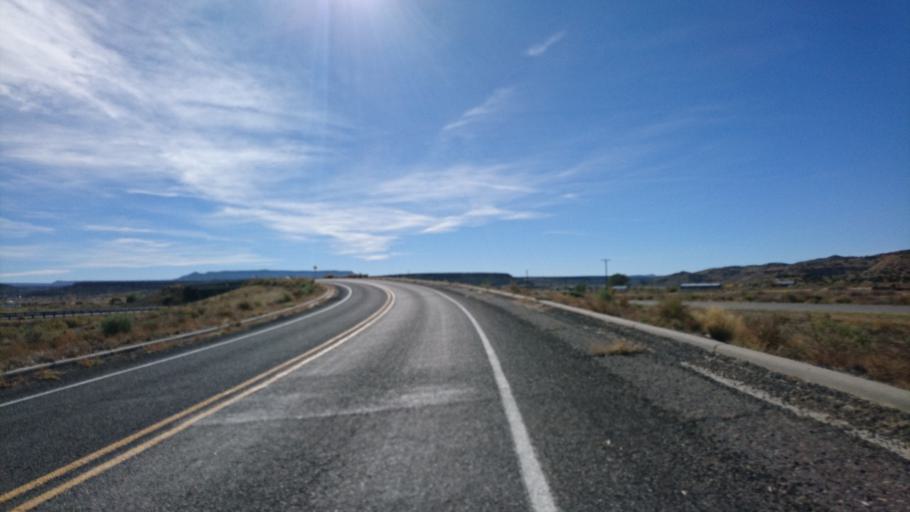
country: US
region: New Mexico
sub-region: Cibola County
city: Skyline-Ganipa
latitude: 35.0760
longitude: -107.6548
